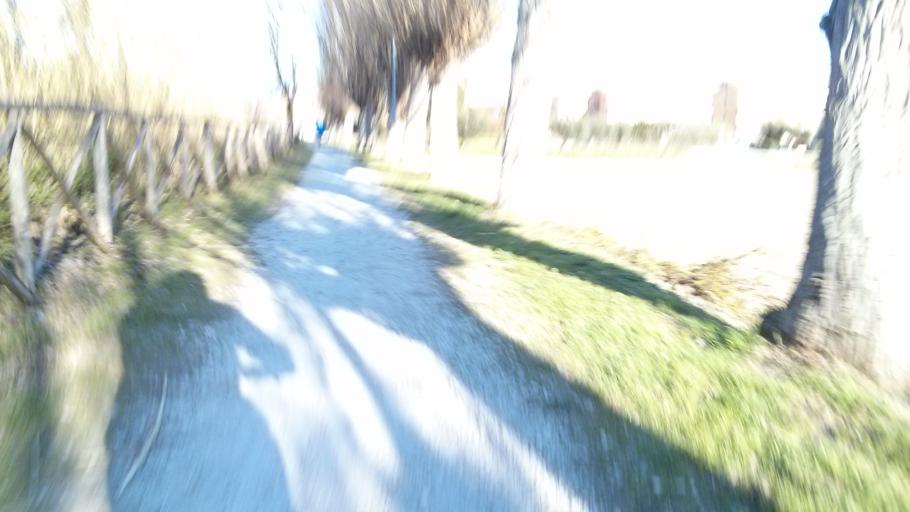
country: IT
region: The Marches
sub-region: Provincia di Pesaro e Urbino
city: Fano
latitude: 43.8509
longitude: 13.0007
